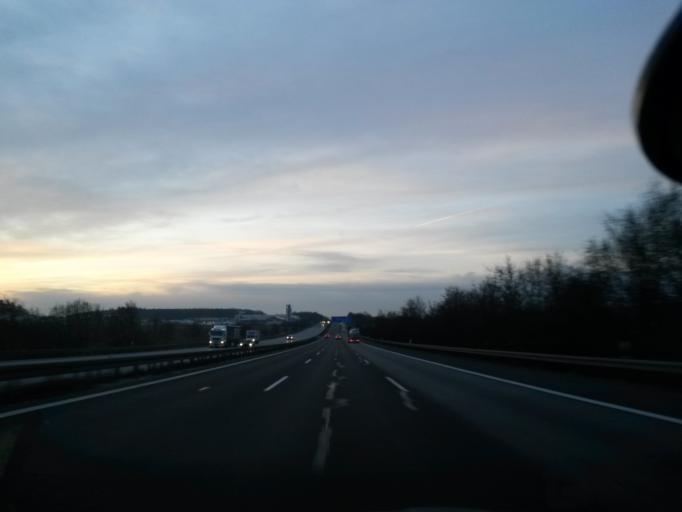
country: DE
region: Bavaria
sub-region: Upper Bavaria
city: Denkendorf
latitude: 48.9380
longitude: 11.4527
